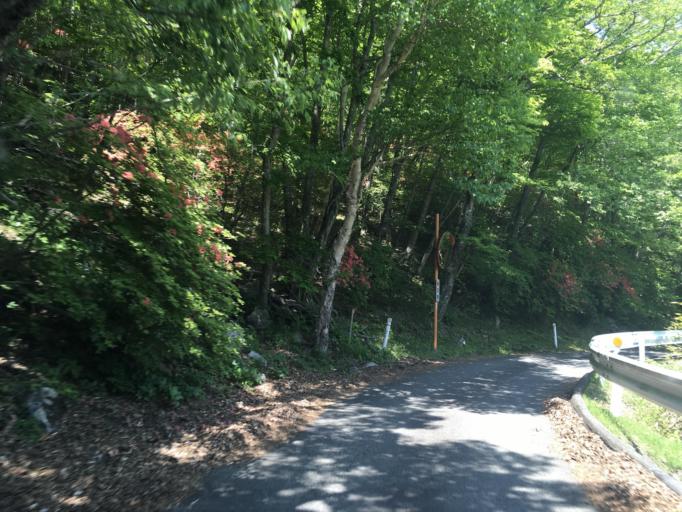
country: JP
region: Iwate
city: Ofunato
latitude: 39.1794
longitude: 141.7396
